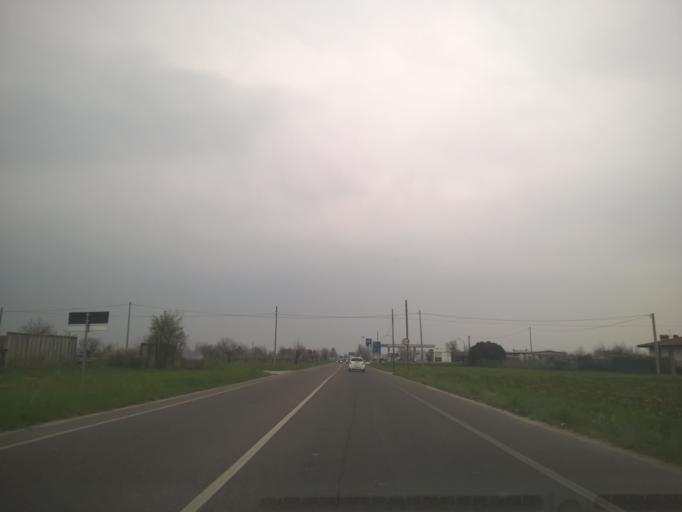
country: IT
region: Veneto
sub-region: Provincia di Vicenza
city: Thiene
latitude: 45.6957
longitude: 11.4623
